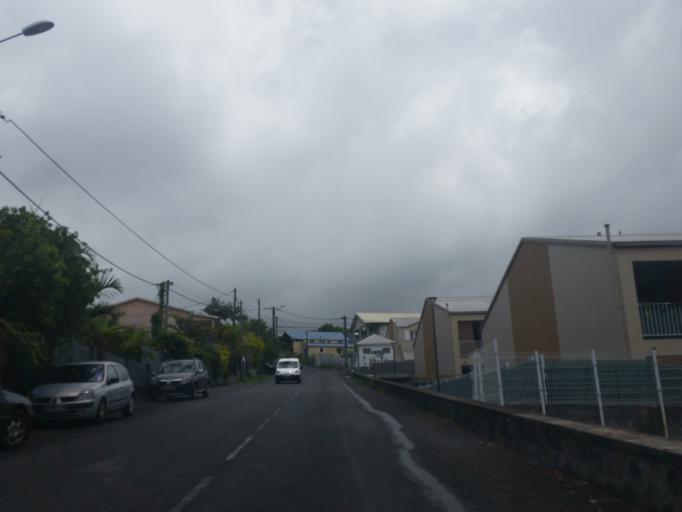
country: RE
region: Reunion
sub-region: Reunion
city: Le Tampon
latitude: -21.2480
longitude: 55.5095
